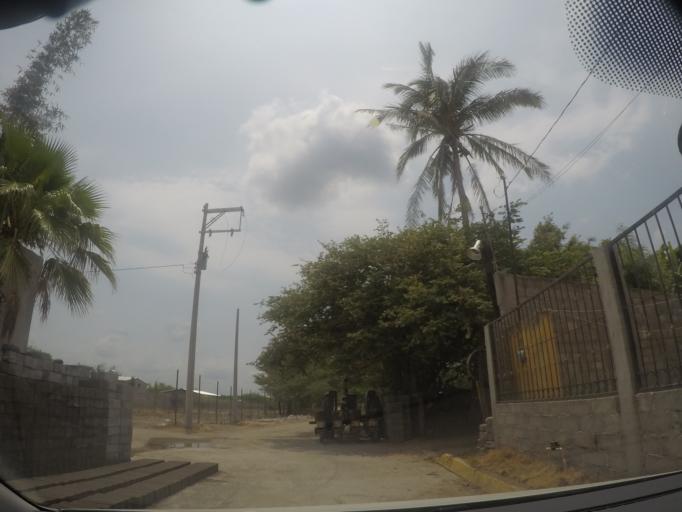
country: MX
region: Oaxaca
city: El Espinal
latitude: 16.4892
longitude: -95.0382
